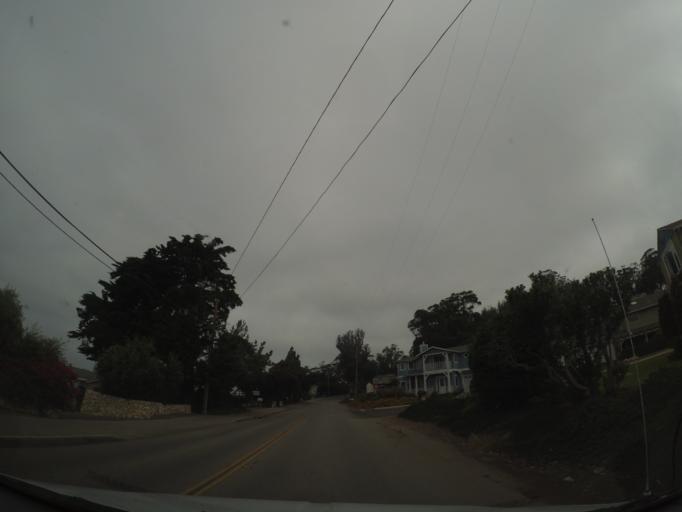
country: US
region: California
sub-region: San Luis Obispo County
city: Morro Bay
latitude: 35.3570
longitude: -120.8476
